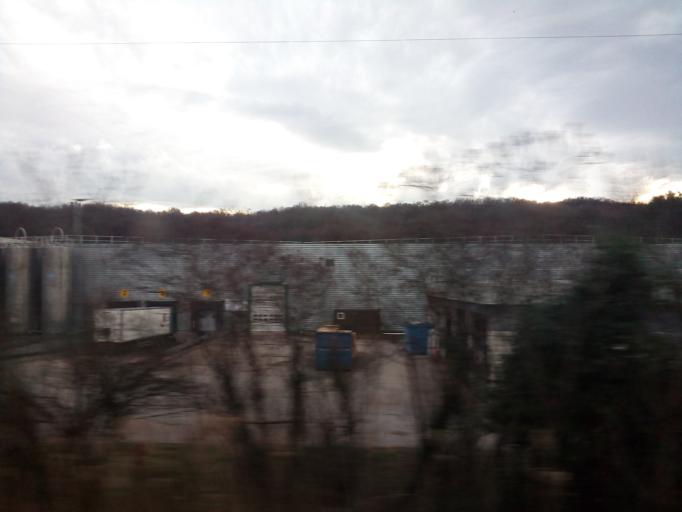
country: FR
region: Rhone-Alpes
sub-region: Departement de l'Isere
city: La Verpilliere
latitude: 45.6286
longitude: 5.1477
